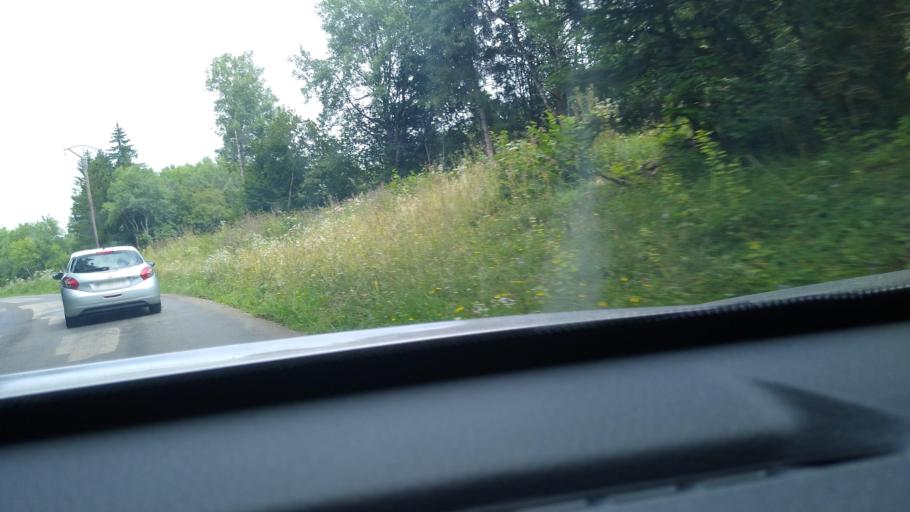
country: FR
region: Rhone-Alpes
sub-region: Departement de l'Ain
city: Saint-Martin-du-Frene
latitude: 46.1335
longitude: 5.5672
